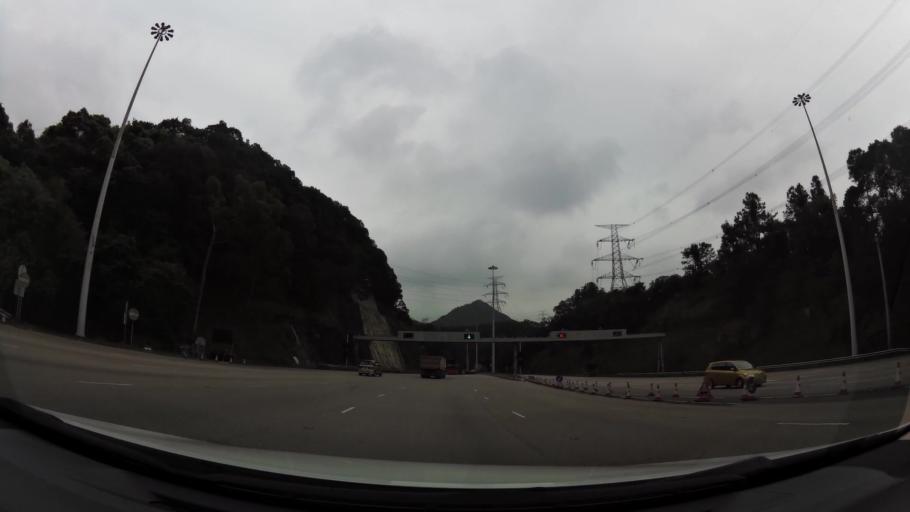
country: HK
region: Tsuen Wan
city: Tsuen Wan
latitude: 22.3812
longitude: 114.1390
